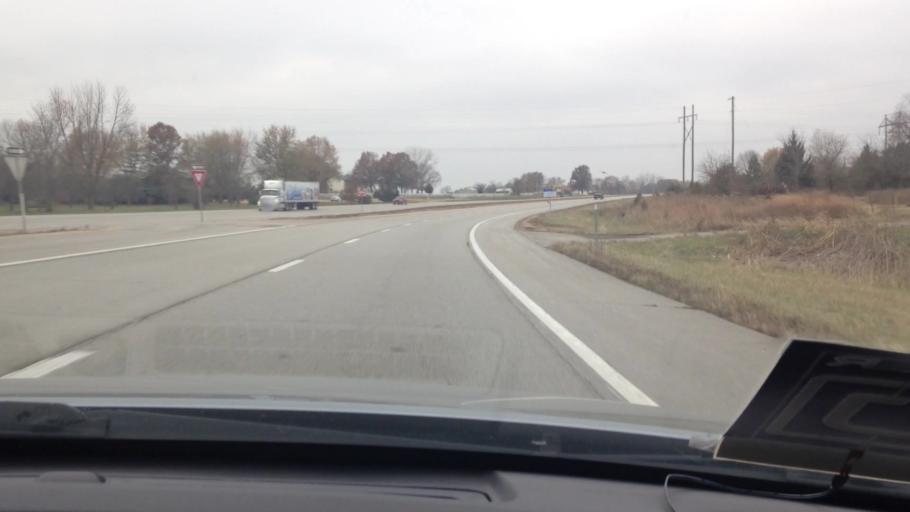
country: US
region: Missouri
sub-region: Cass County
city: Harrisonville
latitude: 38.6098
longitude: -94.3198
